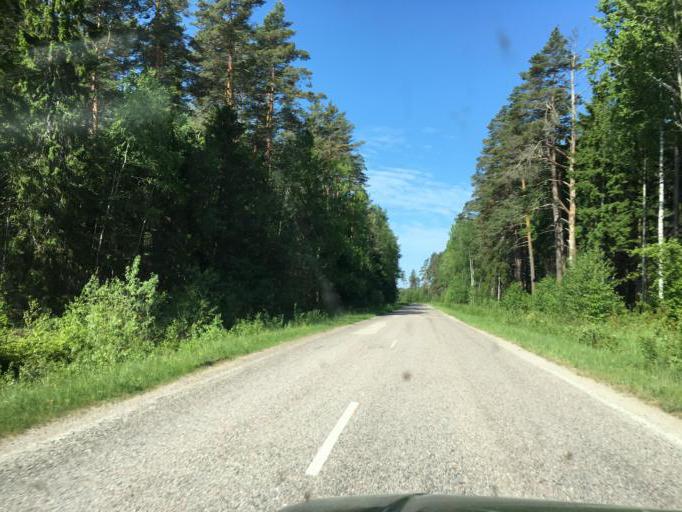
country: LV
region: Ventspils
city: Ventspils
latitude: 57.4921
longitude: 21.8028
